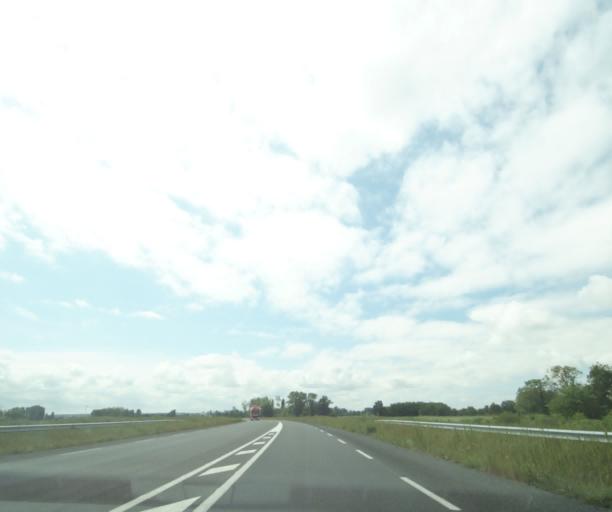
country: FR
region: Poitou-Charentes
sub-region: Departement des Deux-Sevres
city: Sainte-Verge
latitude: 47.0256
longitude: -0.2026
